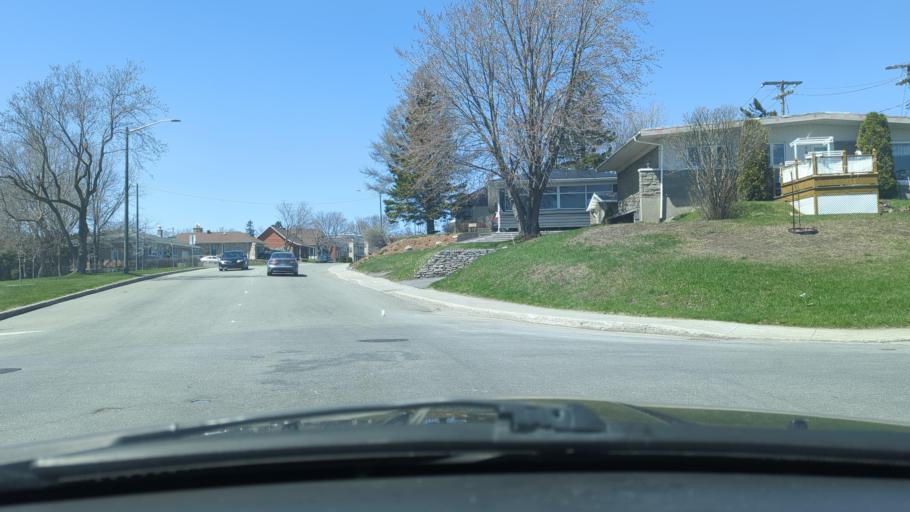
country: CA
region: Quebec
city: Quebec
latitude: 46.8566
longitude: -71.2073
